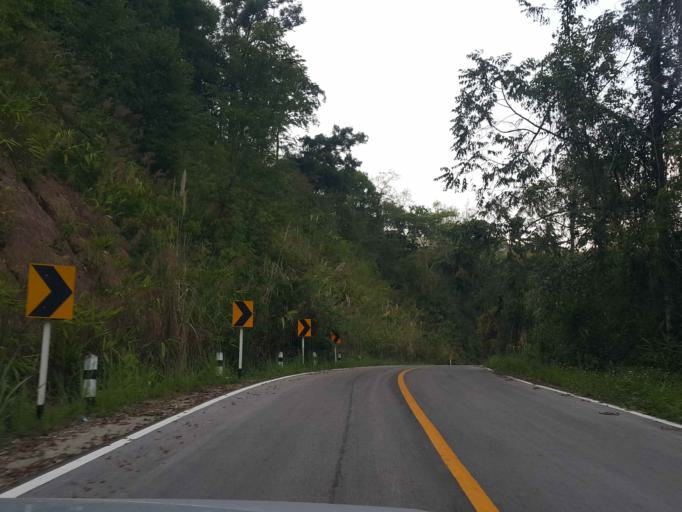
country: TH
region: Chiang Mai
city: Mae On
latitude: 18.9746
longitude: 99.3231
